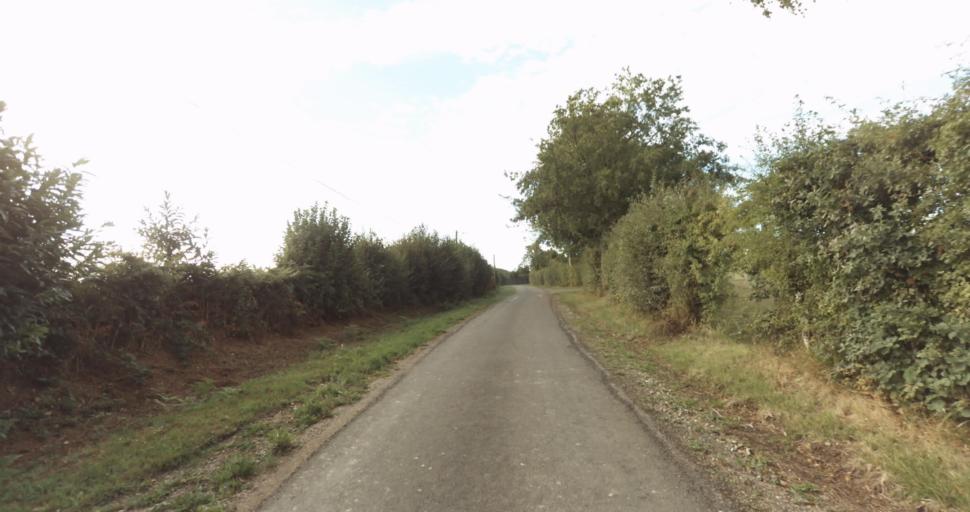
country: FR
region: Lower Normandy
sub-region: Departement de l'Orne
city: Gace
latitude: 48.8300
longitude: 0.2111
